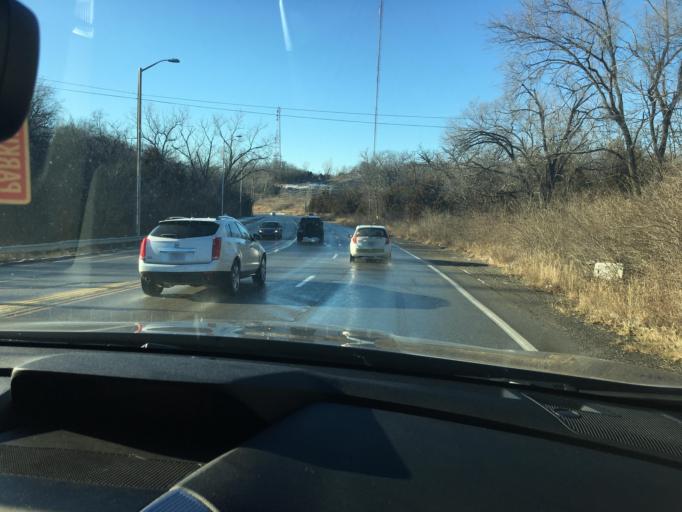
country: US
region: Missouri
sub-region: Jackson County
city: Raytown
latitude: 39.0130
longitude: -94.4997
